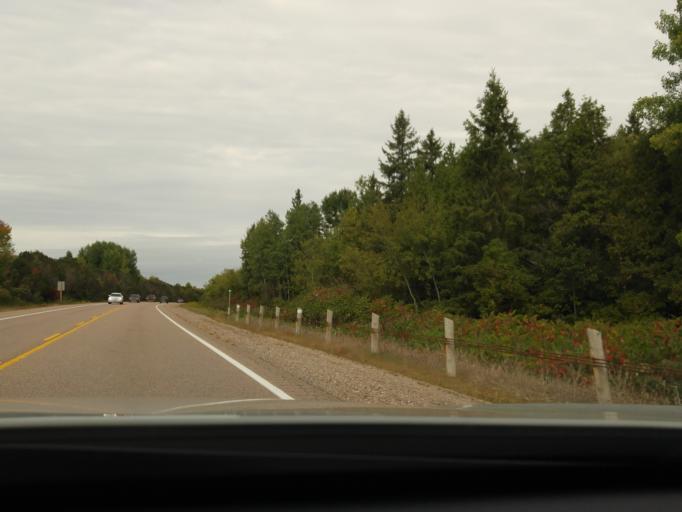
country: CA
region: Ontario
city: Renfrew
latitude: 45.5562
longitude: -76.7423
